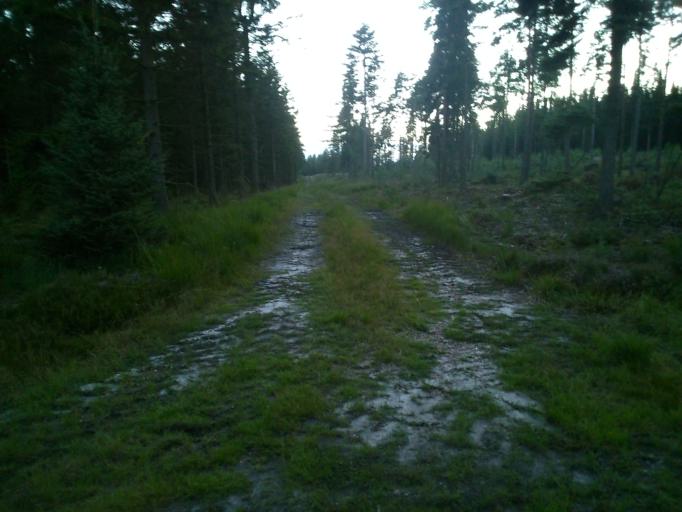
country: DK
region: Central Jutland
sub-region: Ringkobing-Skjern Kommune
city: Skjern
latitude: 56.0165
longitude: 8.4541
